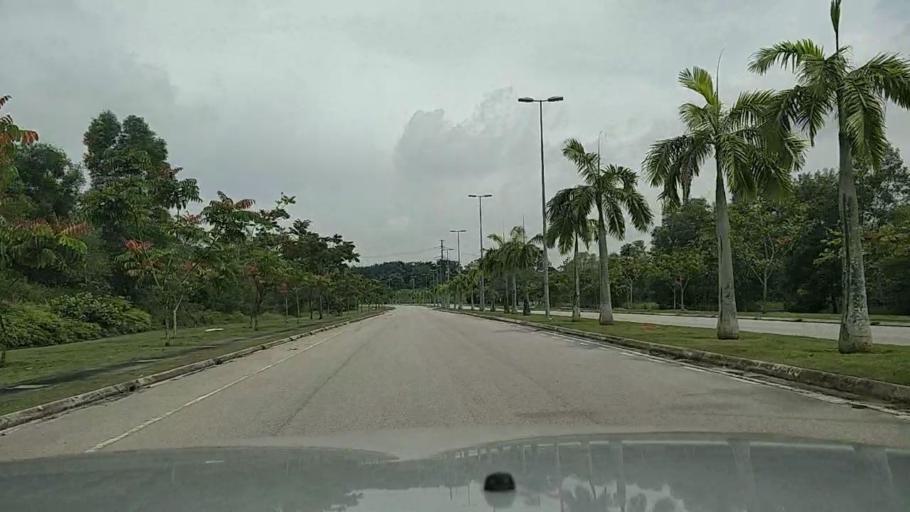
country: MY
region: Putrajaya
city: Putrajaya
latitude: 2.9009
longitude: 101.6490
